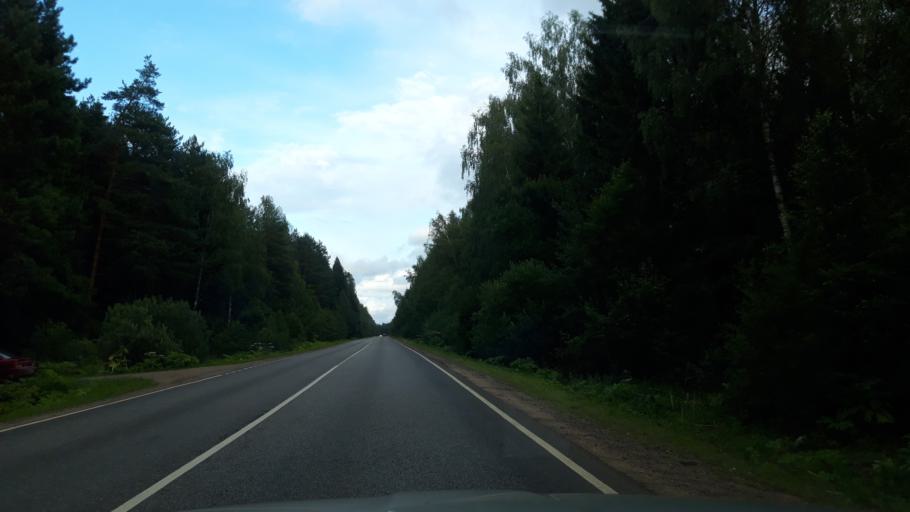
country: RU
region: Moskovskaya
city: Solnechnogorsk
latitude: 56.0961
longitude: 36.8784
